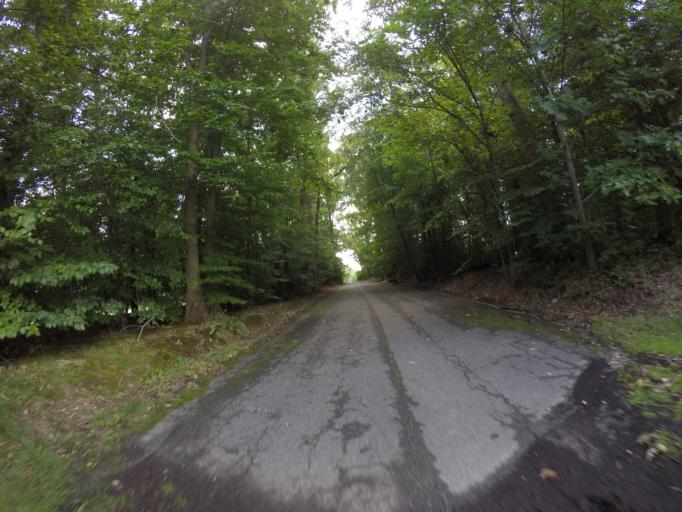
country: US
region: Maryland
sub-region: Anne Arundel County
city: Odenton
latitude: 39.0583
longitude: -76.7026
